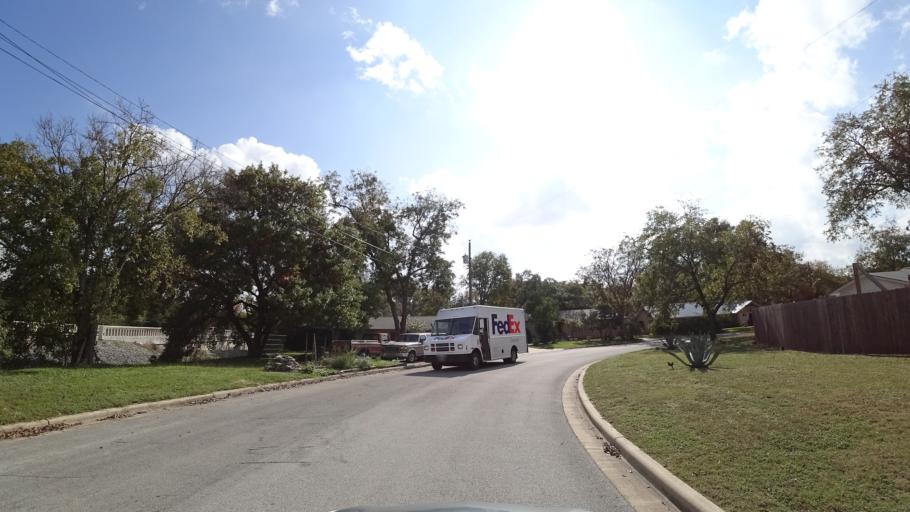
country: US
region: Texas
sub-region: Williamson County
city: Round Rock
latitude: 30.5143
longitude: -97.6816
